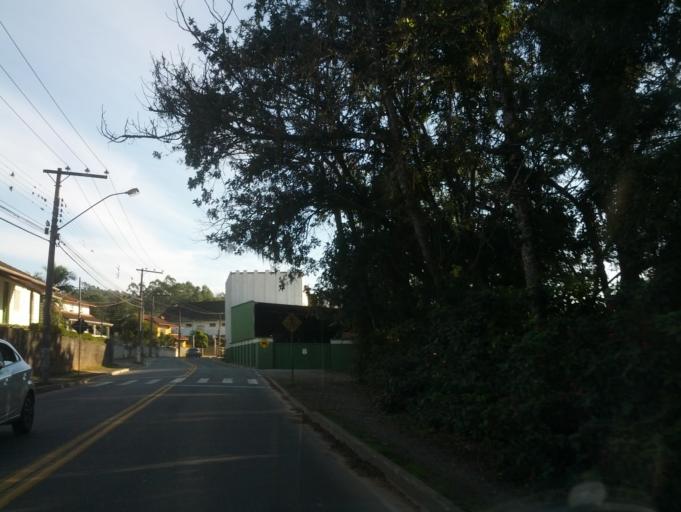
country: BR
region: Santa Catarina
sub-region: Indaial
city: Indaial
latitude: -26.8897
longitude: -49.1905
